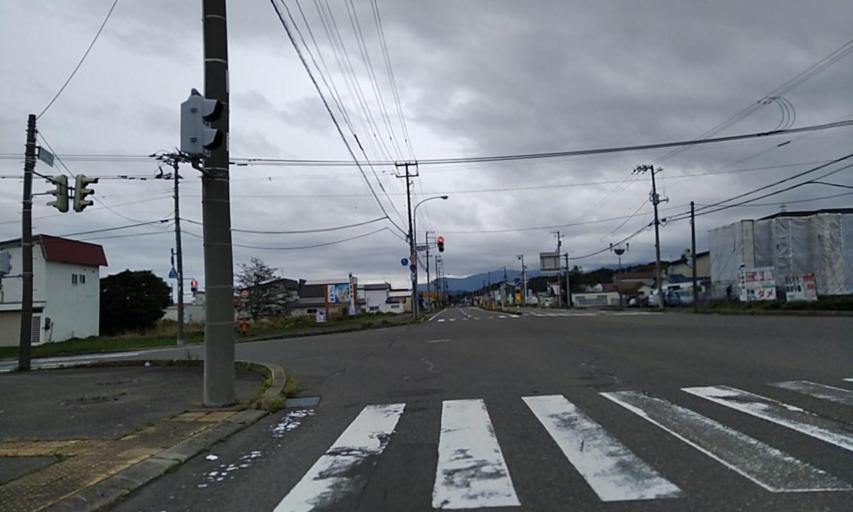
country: JP
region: Hokkaido
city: Obihiro
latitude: 42.3027
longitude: 143.3169
